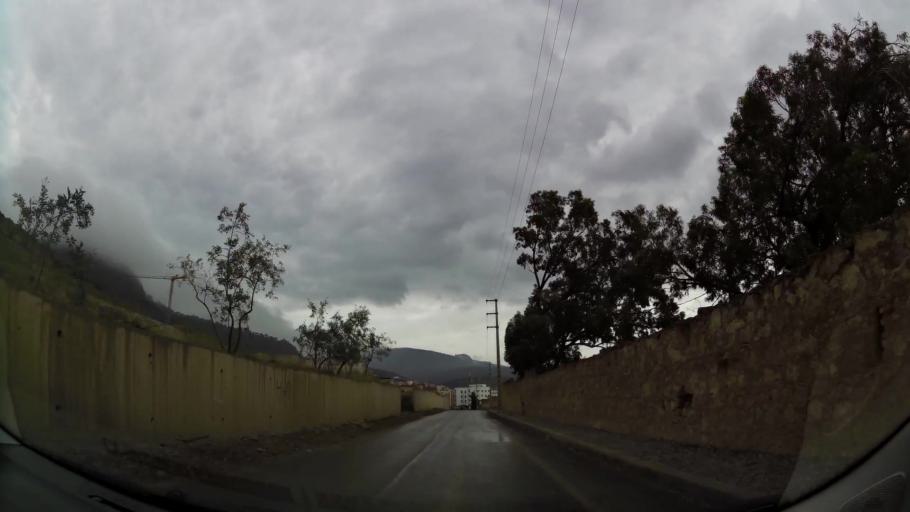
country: MA
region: Oriental
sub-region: Nador
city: Nador
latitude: 35.1499
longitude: -3.0079
